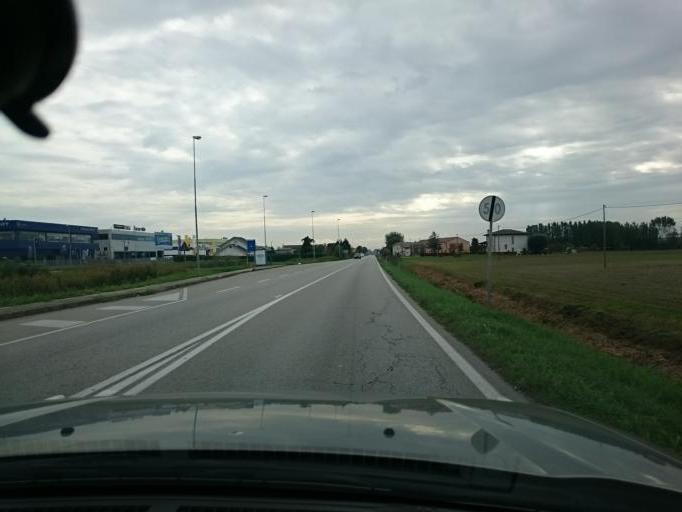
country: IT
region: Veneto
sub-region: Provincia di Padova
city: Sant'Angelo di Piove di Sacco
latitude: 45.3157
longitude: 12.0075
